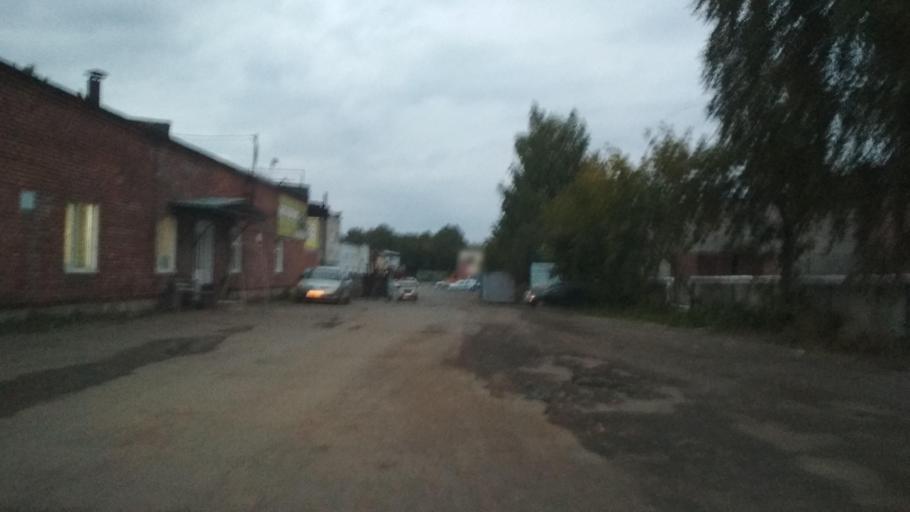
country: RU
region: Tomsk
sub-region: Tomskiy Rayon
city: Tomsk
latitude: 56.4780
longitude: 85.0179
